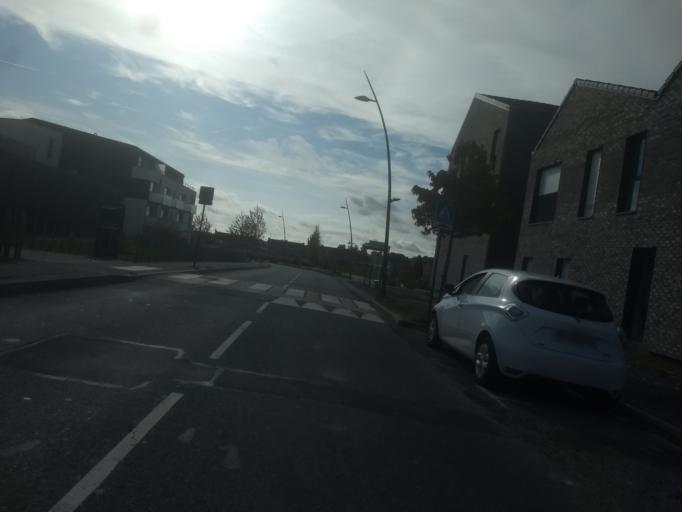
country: FR
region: Nord-Pas-de-Calais
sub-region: Departement du Pas-de-Calais
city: Dainville
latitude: 50.2899
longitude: 2.7360
